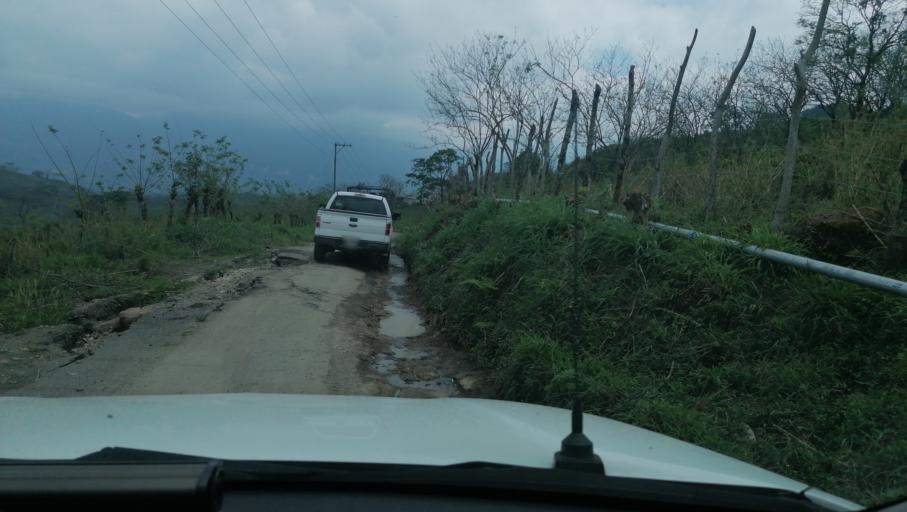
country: MX
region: Chiapas
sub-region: Francisco Leon
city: San Miguel la Sardina
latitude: 17.2744
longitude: -93.2681
